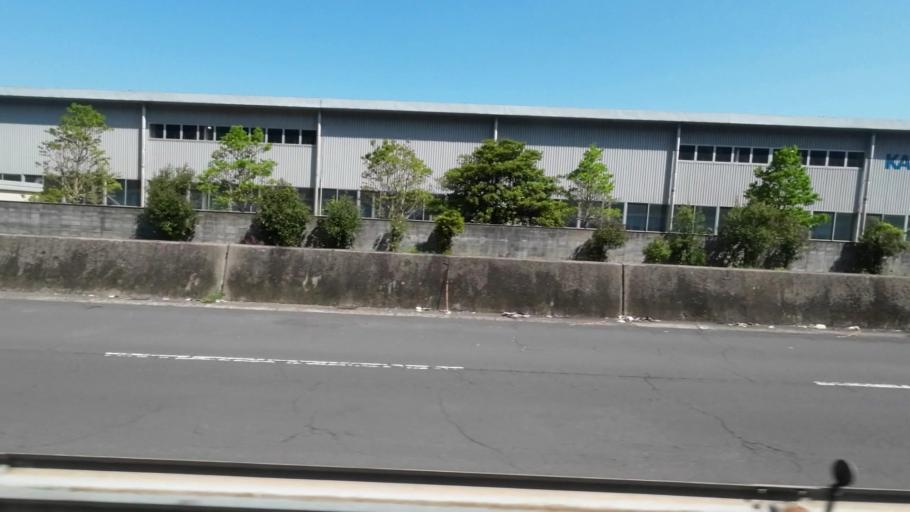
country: JP
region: Ehime
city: Kawanoecho
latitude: 34.0416
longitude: 133.6067
